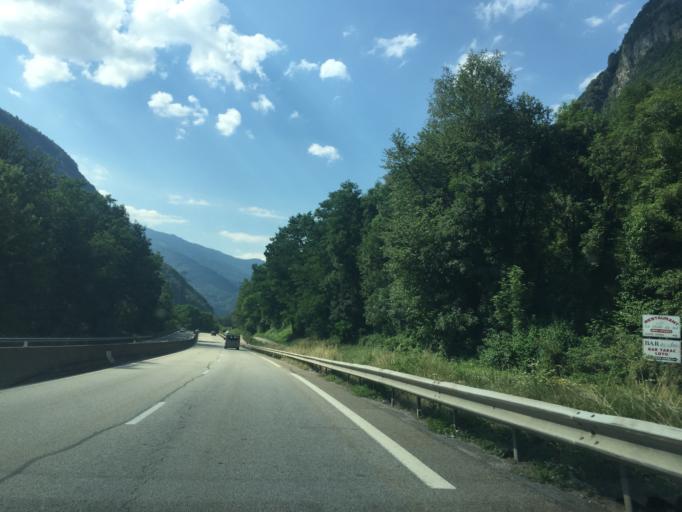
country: FR
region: Rhone-Alpes
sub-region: Departement de la Savoie
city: La Bathie
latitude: 45.5679
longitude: 6.4680
